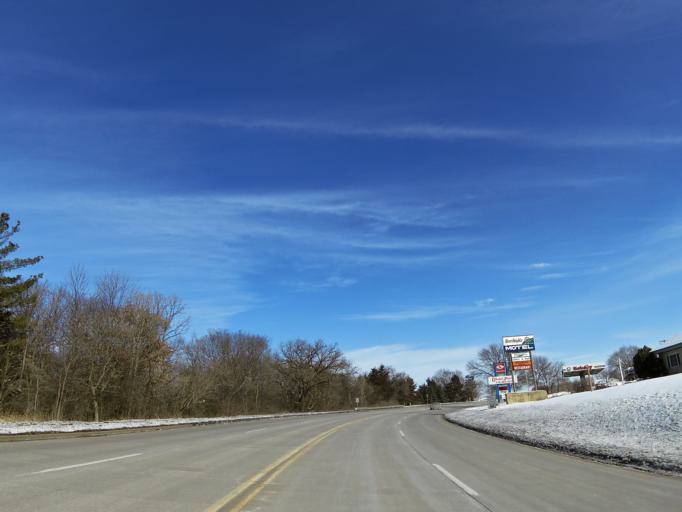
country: US
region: Wisconsin
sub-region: Pierce County
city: Prescott
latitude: 44.7590
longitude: -92.8023
